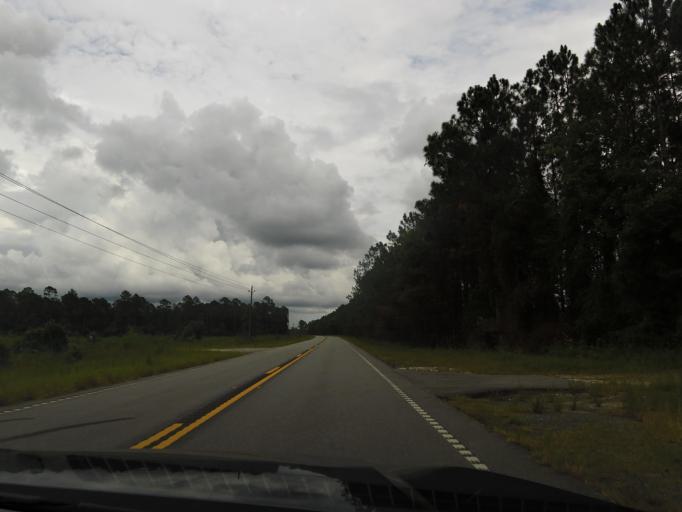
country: US
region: Florida
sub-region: Baker County
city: Macclenny
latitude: 30.5223
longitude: -82.1935
